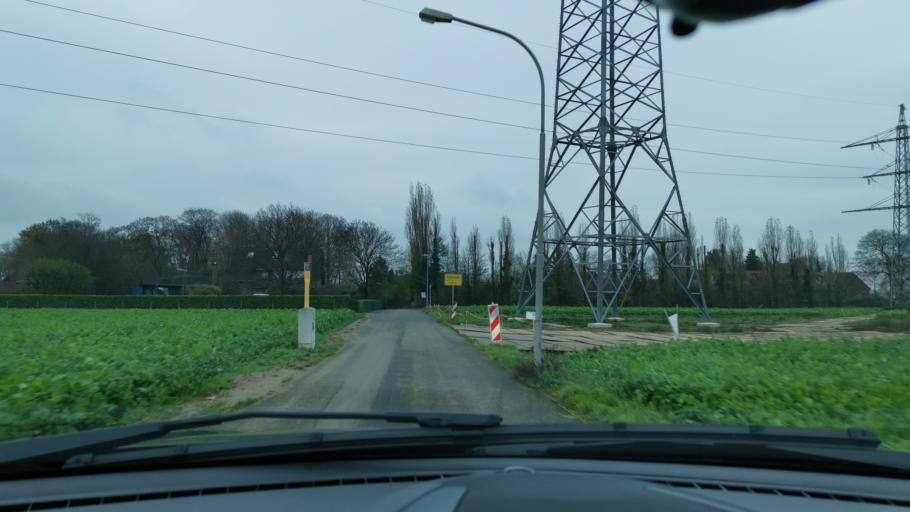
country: DE
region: North Rhine-Westphalia
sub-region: Regierungsbezirk Dusseldorf
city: Neubrueck
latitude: 51.1167
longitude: 6.6982
